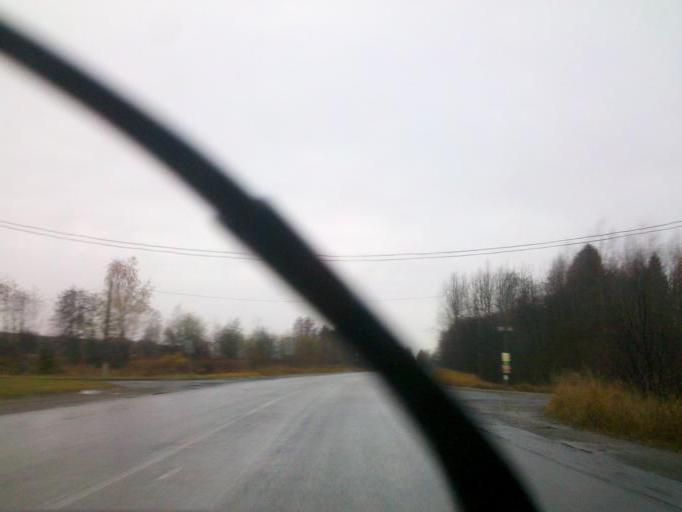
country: RU
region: Republic of Karelia
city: Petrozavodsk
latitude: 61.8210
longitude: 34.2431
